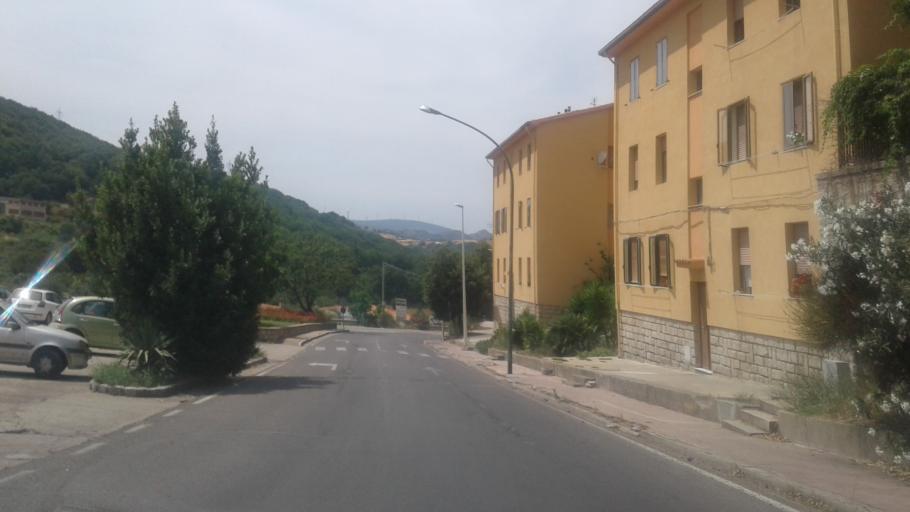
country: IT
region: Sardinia
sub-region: Provincia di Olbia-Tempio
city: Tempio Pausania
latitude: 40.9053
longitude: 9.0977
